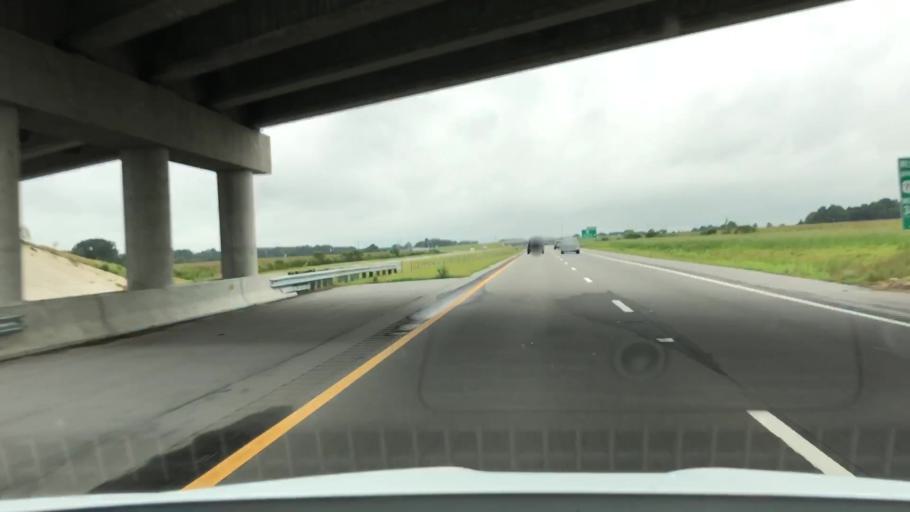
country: US
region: North Carolina
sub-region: Wayne County
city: Elroy
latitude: 35.4086
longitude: -77.8891
